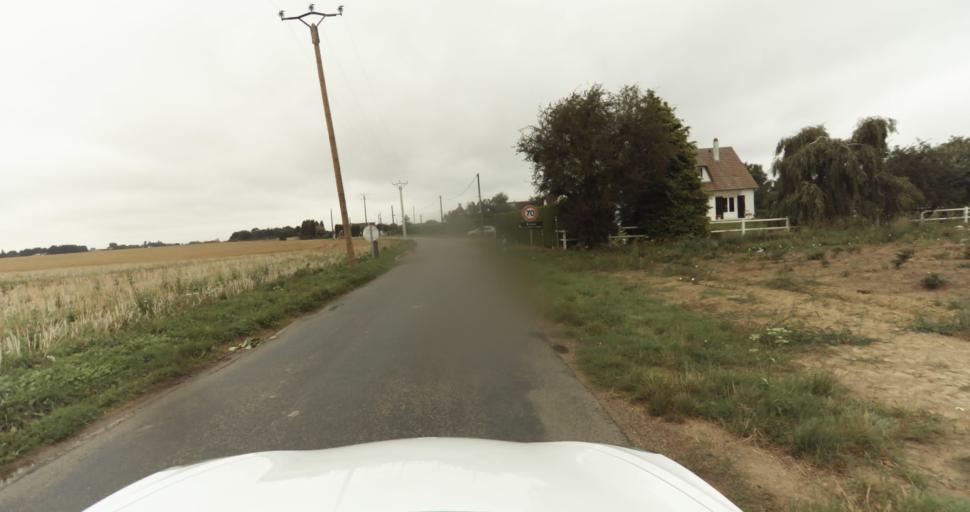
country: FR
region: Haute-Normandie
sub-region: Departement de l'Eure
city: Aviron
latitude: 49.0671
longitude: 1.1168
